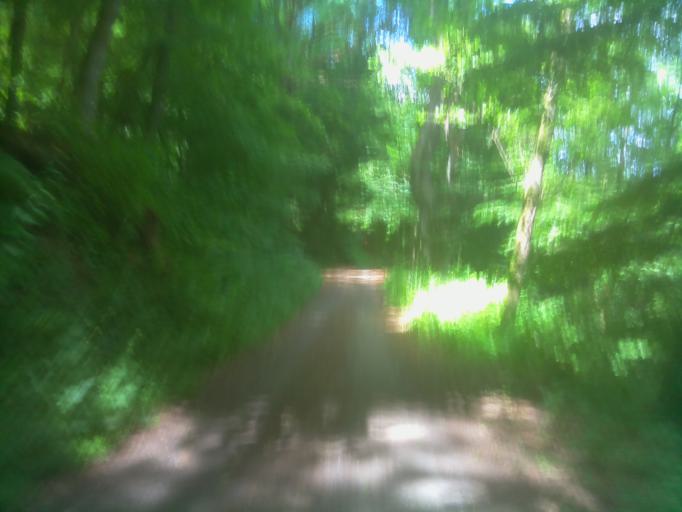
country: DE
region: Hesse
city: Hirschhorn
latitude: 49.4430
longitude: 8.9039
